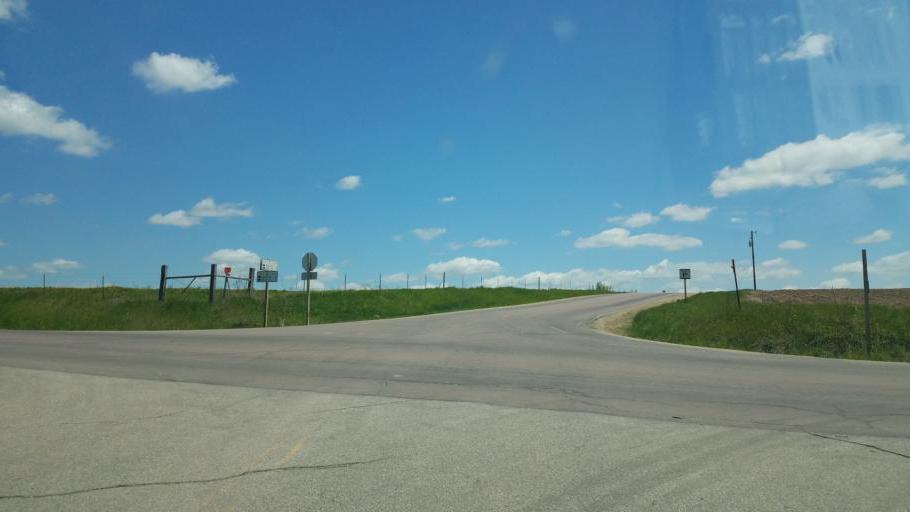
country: US
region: Wisconsin
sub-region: Vernon County
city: Hillsboro
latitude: 43.6461
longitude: -90.4526
